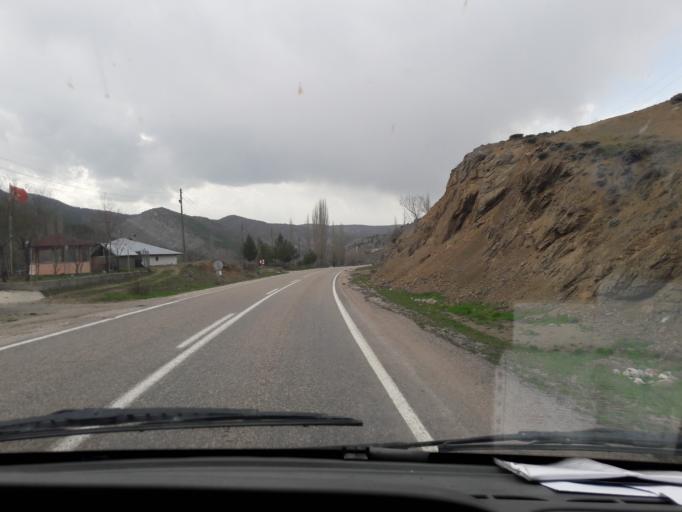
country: TR
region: Giresun
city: Alucra
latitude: 40.2744
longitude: 38.8484
